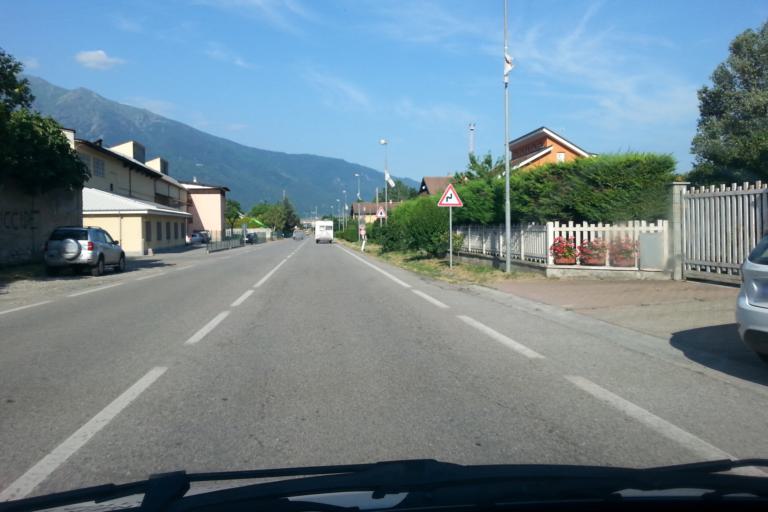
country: IT
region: Piedmont
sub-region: Provincia di Torino
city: Bussoleno
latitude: 45.1380
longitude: 7.1275
